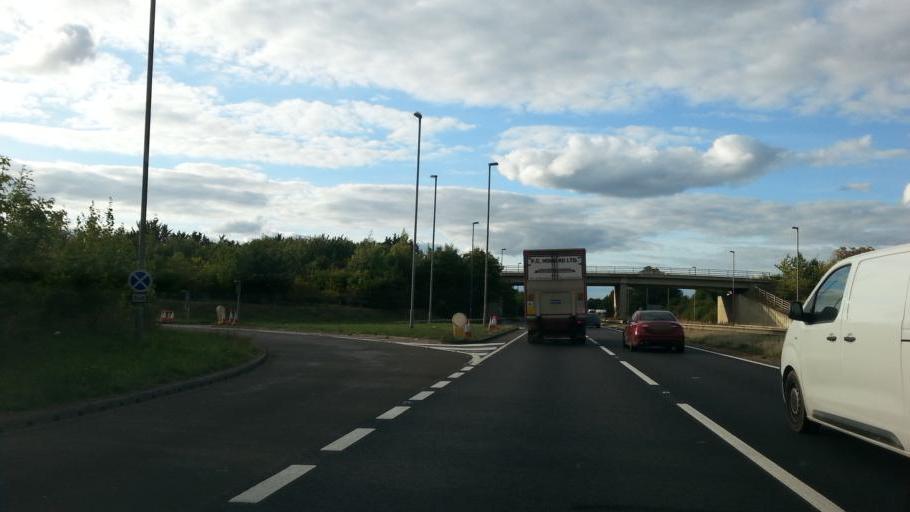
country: GB
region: England
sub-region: Peterborough
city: Wansford
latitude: 52.5717
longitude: -0.3980
